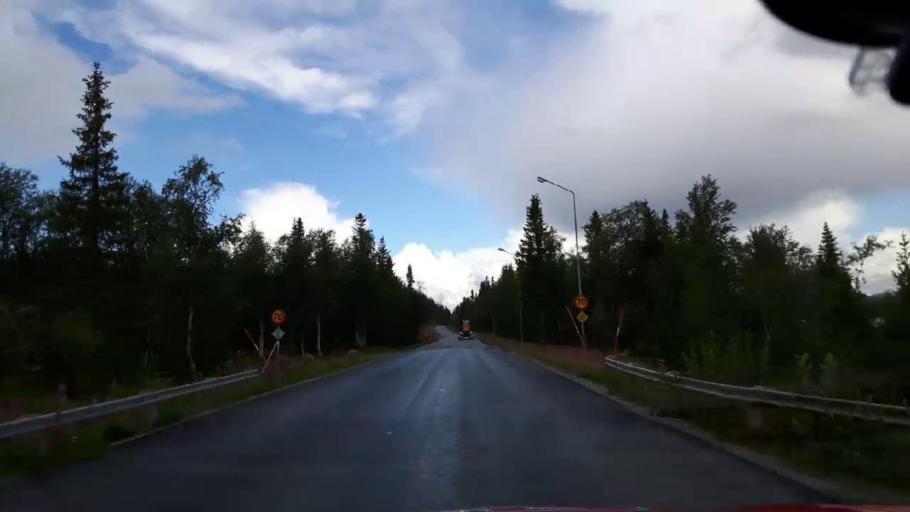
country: SE
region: Vaesterbotten
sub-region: Vilhelmina Kommun
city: Sjoberg
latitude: 64.9733
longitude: 15.3313
